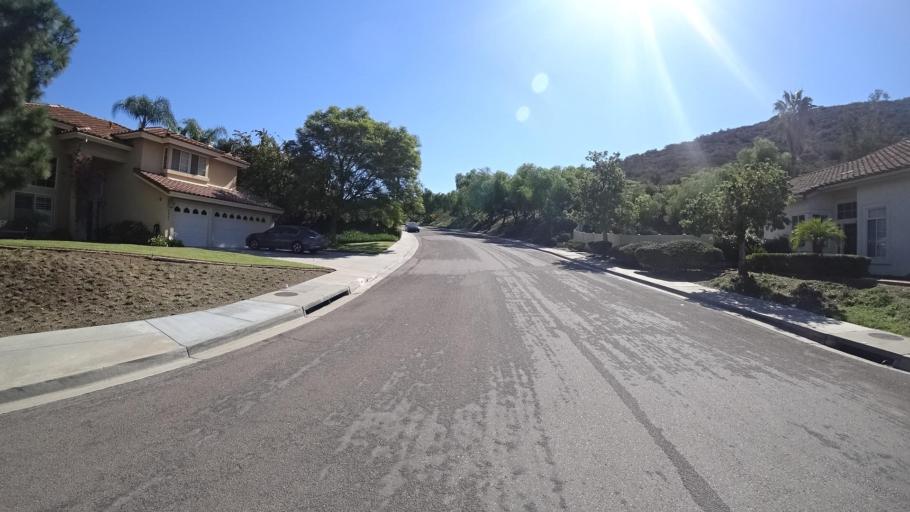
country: US
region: California
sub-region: San Diego County
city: Rancho San Diego
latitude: 32.7350
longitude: -116.9166
